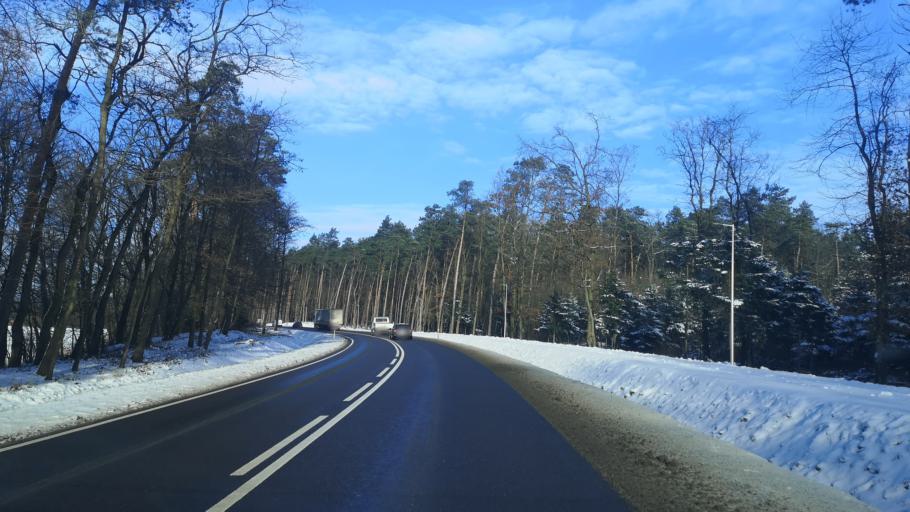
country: PL
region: Subcarpathian Voivodeship
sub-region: Powiat przeworski
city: Tryncza
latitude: 50.1274
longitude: 22.5367
